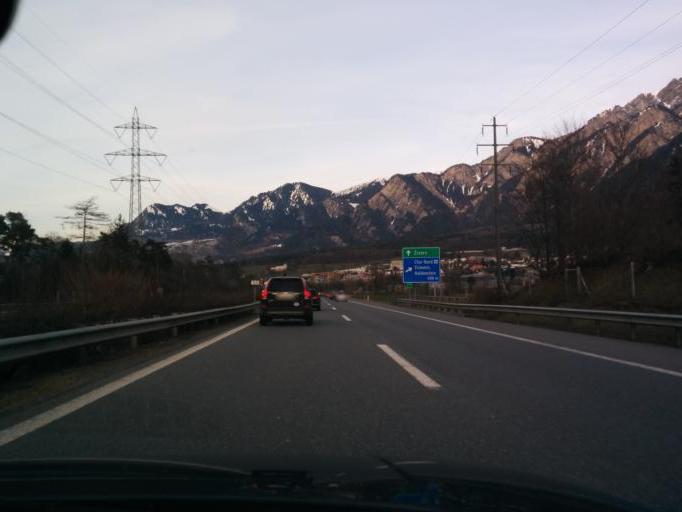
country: CH
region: Grisons
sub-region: Plessur District
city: Chur
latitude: 46.8683
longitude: 9.5220
